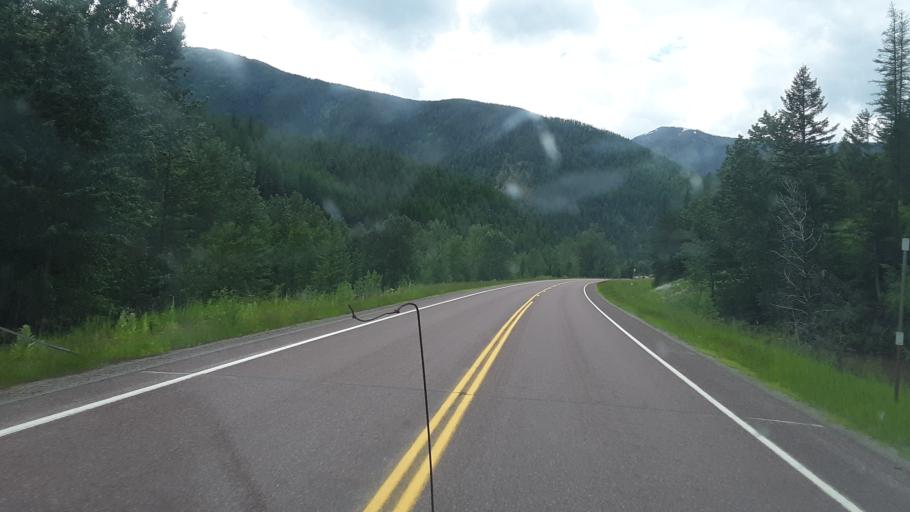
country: US
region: Montana
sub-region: Flathead County
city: Bigfork
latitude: 48.2328
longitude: -113.5522
